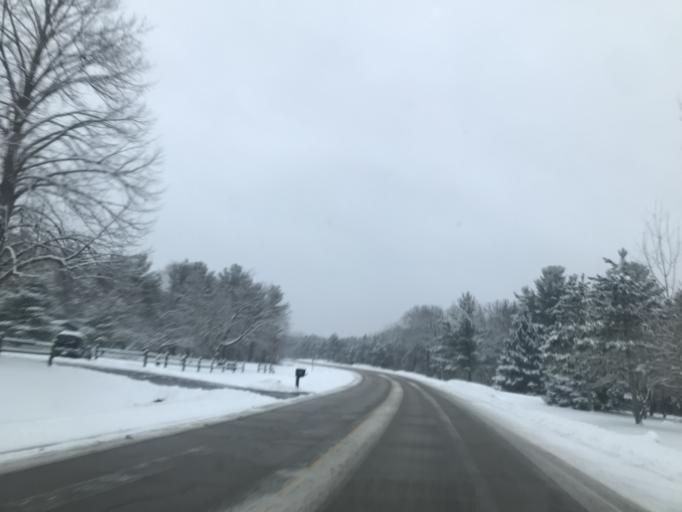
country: US
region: Wisconsin
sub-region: Oconto County
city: Oconto Falls
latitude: 44.8647
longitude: -88.1251
